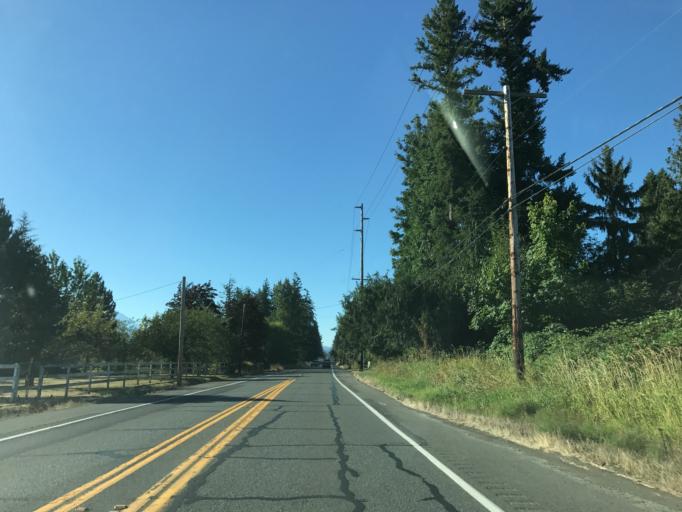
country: US
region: Washington
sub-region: King County
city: Enumclaw
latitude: 47.2409
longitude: -121.9897
